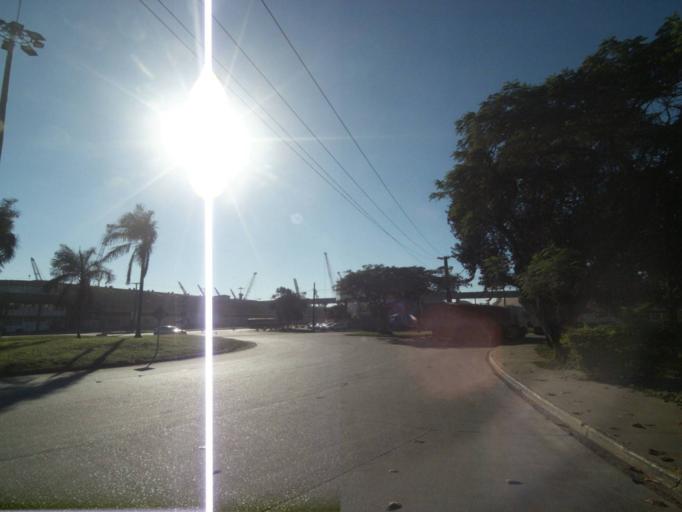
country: BR
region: Parana
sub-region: Paranagua
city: Paranagua
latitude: -25.5046
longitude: -48.5146
